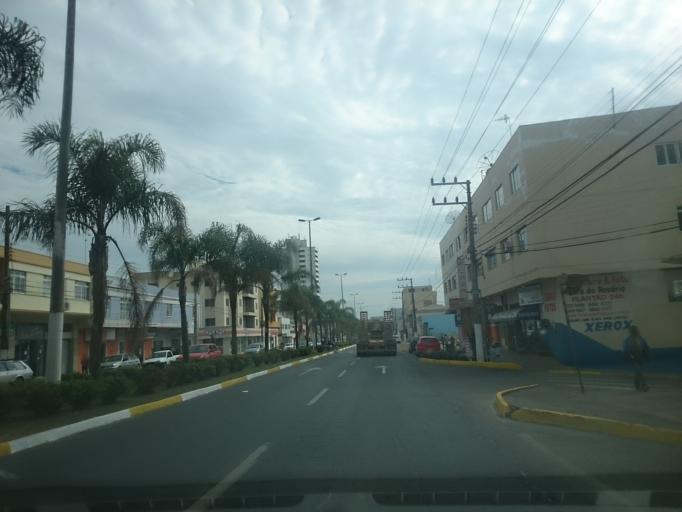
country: BR
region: Santa Catarina
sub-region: Lages
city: Lages
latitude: -27.8053
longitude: -50.3046
